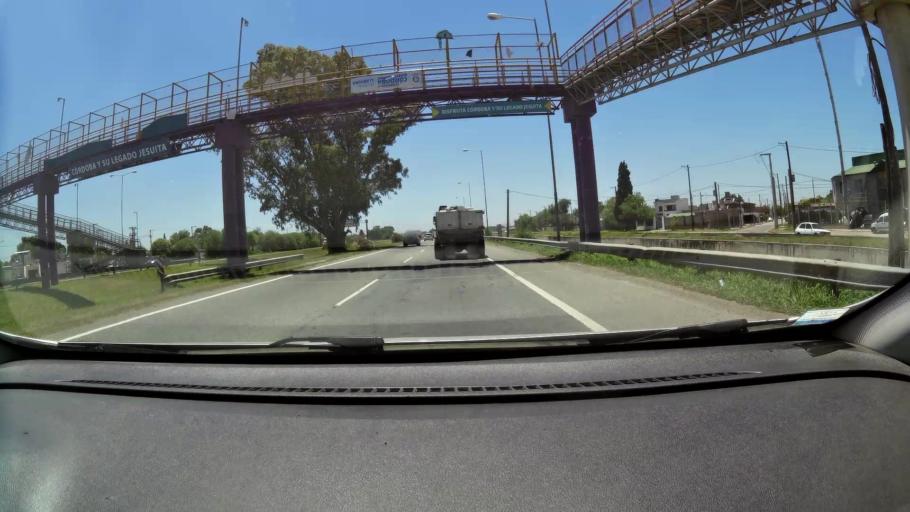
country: AR
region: Cordoba
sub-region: Departamento de Capital
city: Cordoba
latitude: -31.4363
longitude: -64.1167
